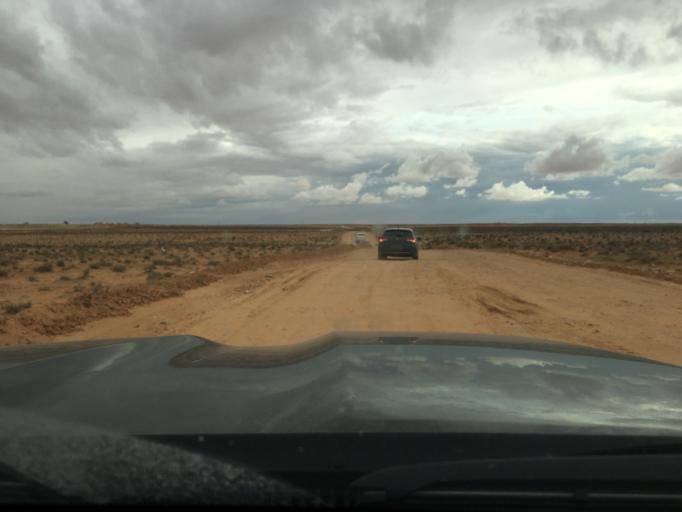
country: TN
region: Madanin
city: Medenine
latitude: 33.2642
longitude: 10.5709
